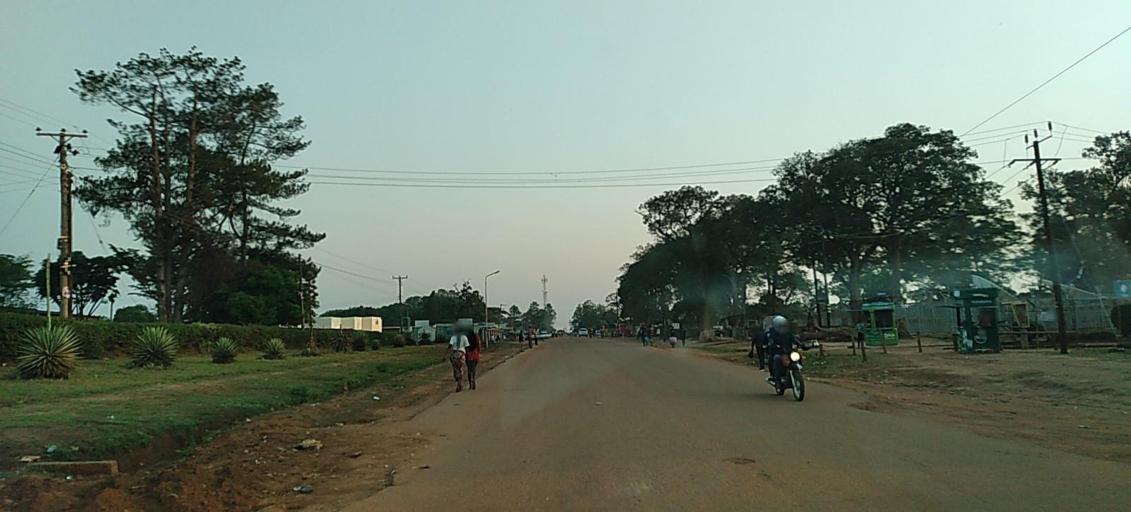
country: ZM
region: North-Western
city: Mwinilunga
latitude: -11.7337
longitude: 24.4311
